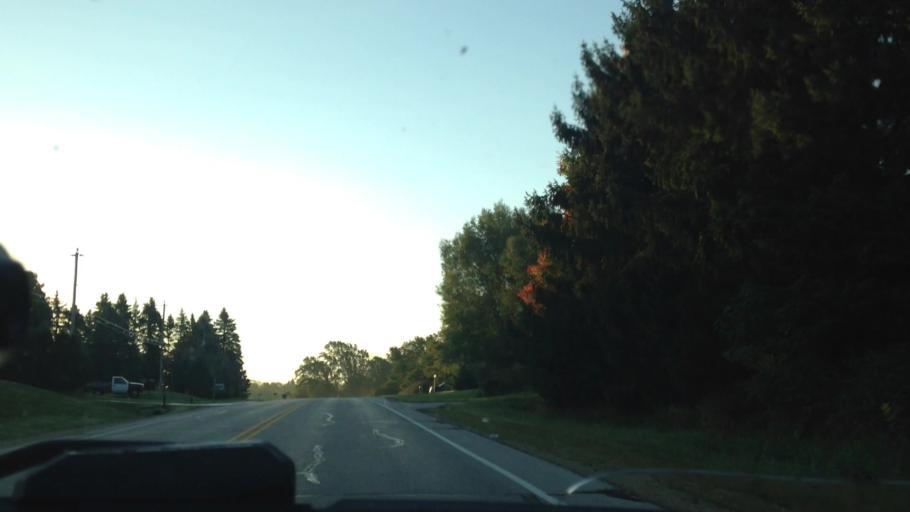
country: US
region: Wisconsin
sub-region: Washington County
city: Newburg
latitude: 43.4241
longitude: -88.0755
